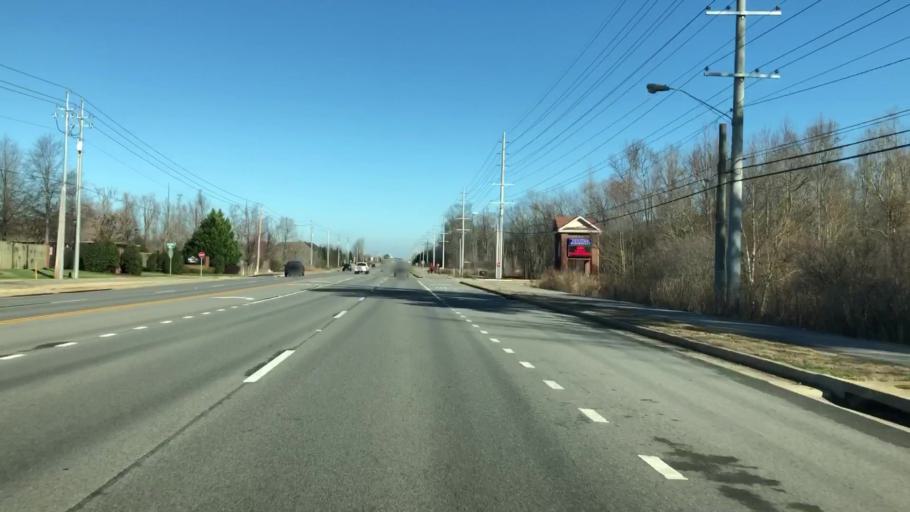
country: US
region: Alabama
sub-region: Madison County
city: Madison
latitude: 34.7198
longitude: -86.7864
